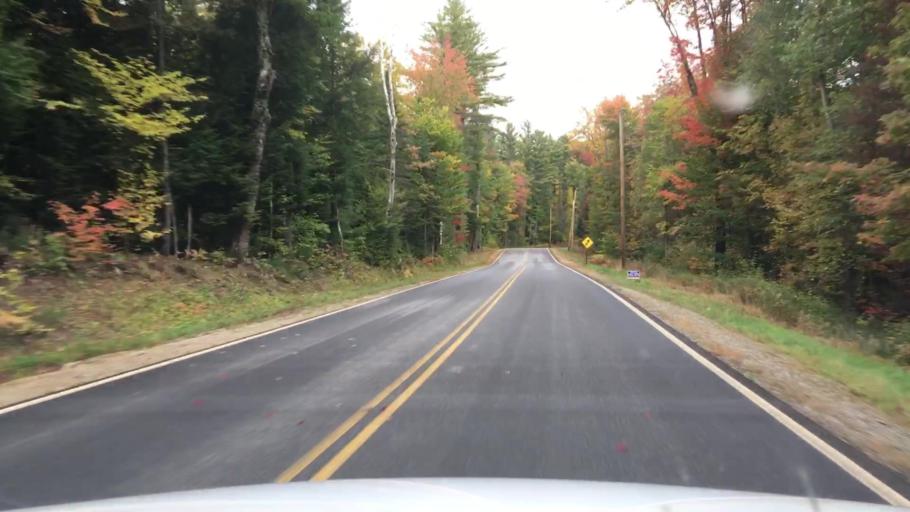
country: US
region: Maine
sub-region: Oxford County
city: Bethel
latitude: 44.2726
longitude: -70.7297
